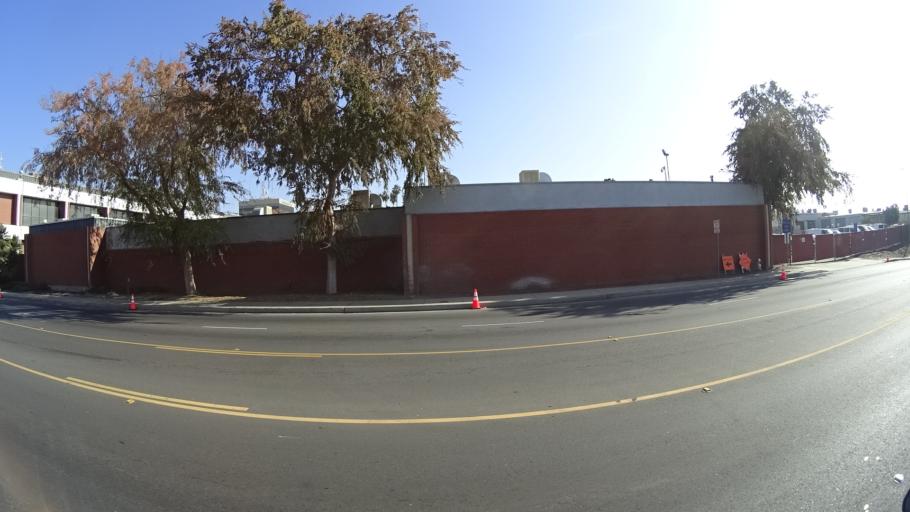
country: US
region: California
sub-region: Kern County
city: Bakersfield
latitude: 35.3727
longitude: -119.0213
